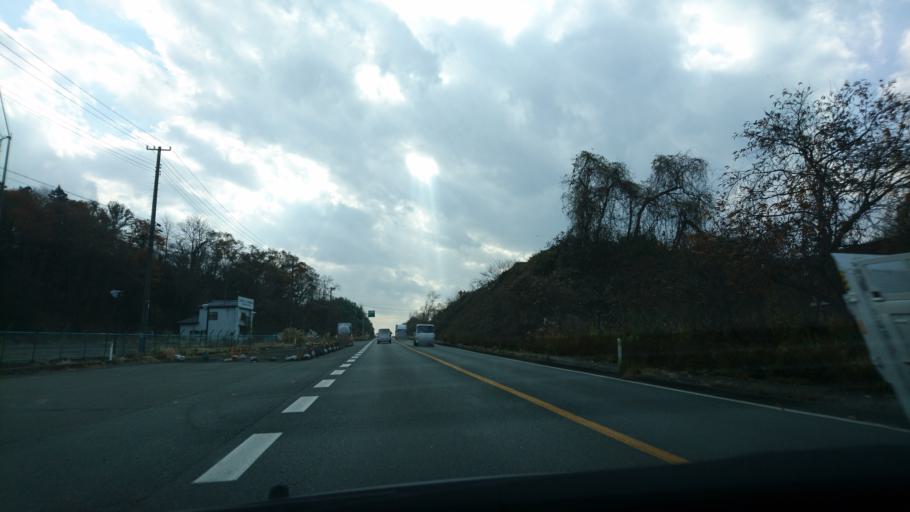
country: JP
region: Iwate
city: Mizusawa
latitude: 39.0311
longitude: 141.1175
